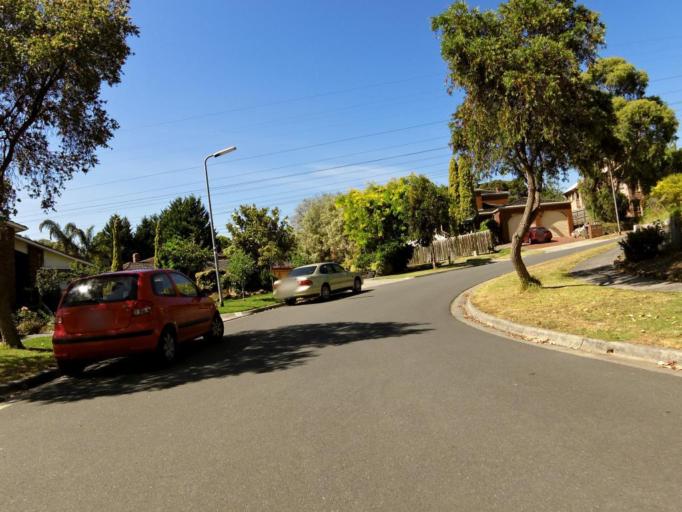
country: AU
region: Victoria
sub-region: Monash
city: Mulgrave
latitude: -37.8973
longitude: 145.1850
